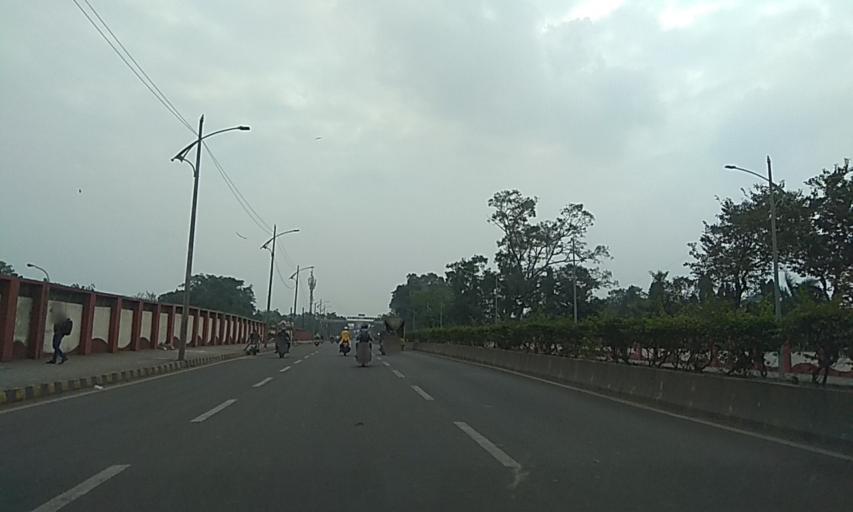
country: IN
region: Maharashtra
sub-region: Pune Division
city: Khadki
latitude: 18.5516
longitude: 73.8659
